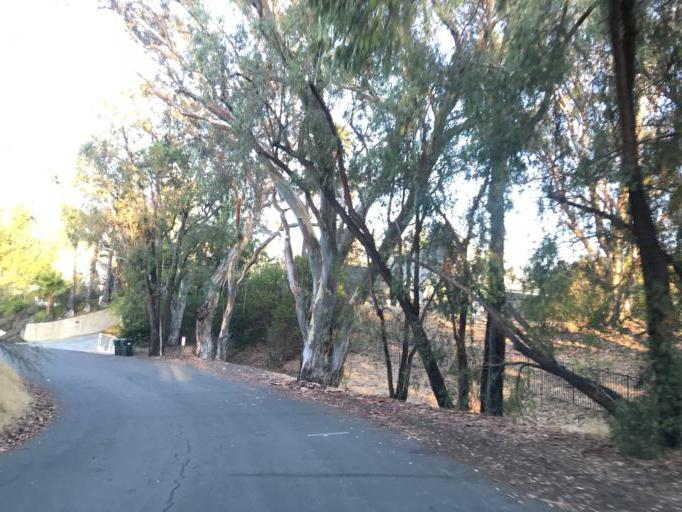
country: US
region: California
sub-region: Los Angeles County
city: Hidden Hills
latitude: 34.1000
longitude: -118.6709
